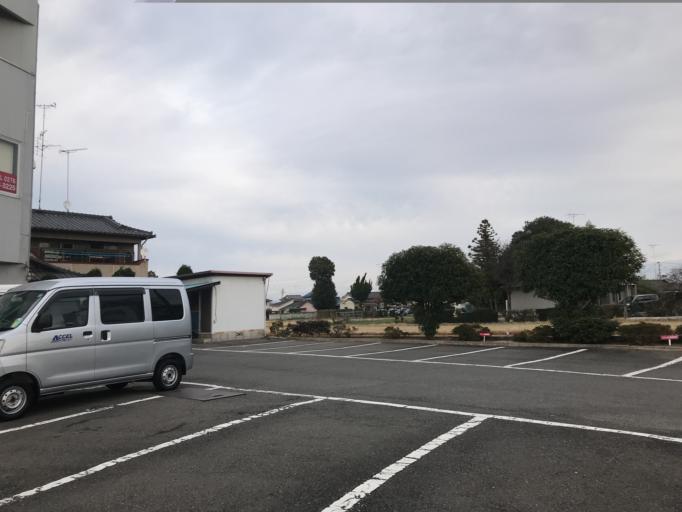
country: JP
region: Gunma
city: Ota
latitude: 36.3070
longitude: 139.3963
